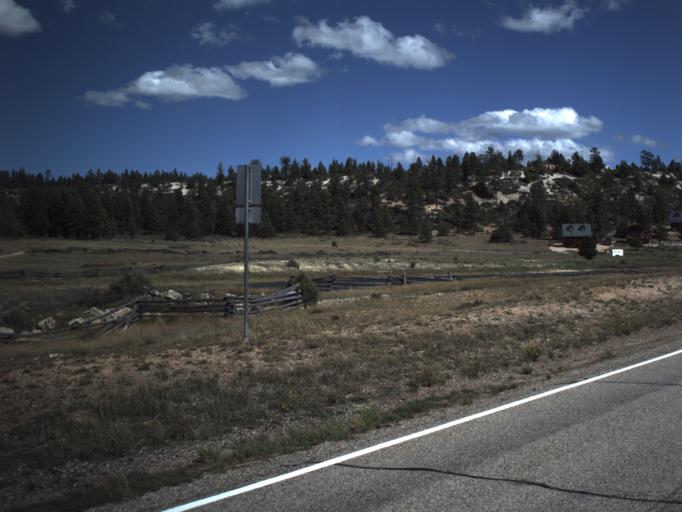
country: US
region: Utah
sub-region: Garfield County
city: Panguitch
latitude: 37.4954
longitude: -112.5802
